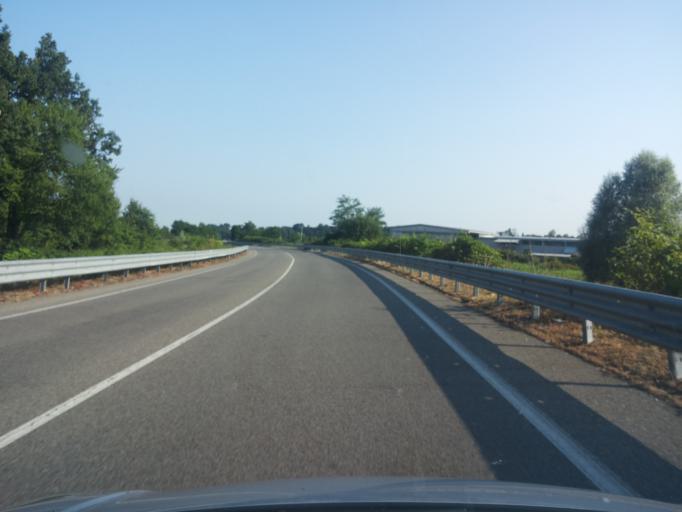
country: IT
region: Piedmont
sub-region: Provincia di Biella
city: Mottalciata
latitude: 45.5101
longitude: 8.2116
